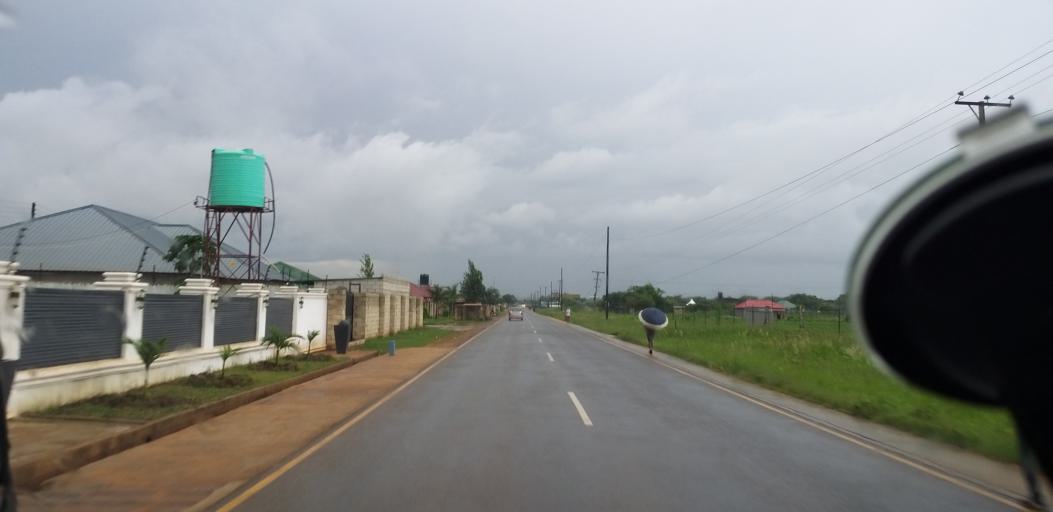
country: ZM
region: Lusaka
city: Lusaka
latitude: -15.5020
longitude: 28.3123
